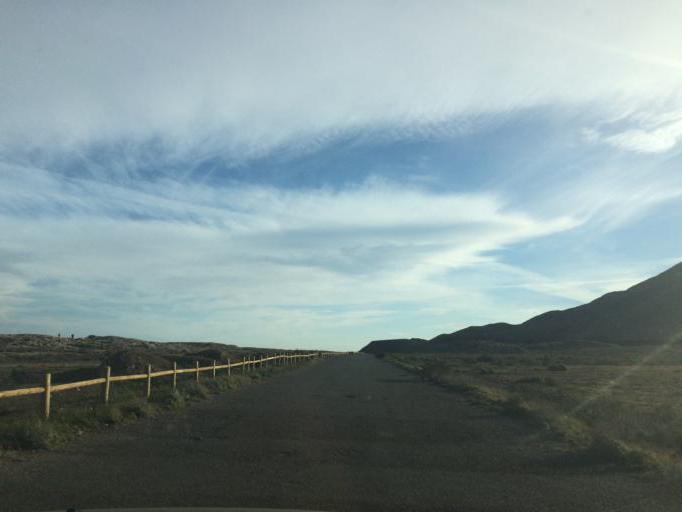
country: ES
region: Andalusia
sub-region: Provincia de Almeria
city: San Jose
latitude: 36.8006
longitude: -2.0638
